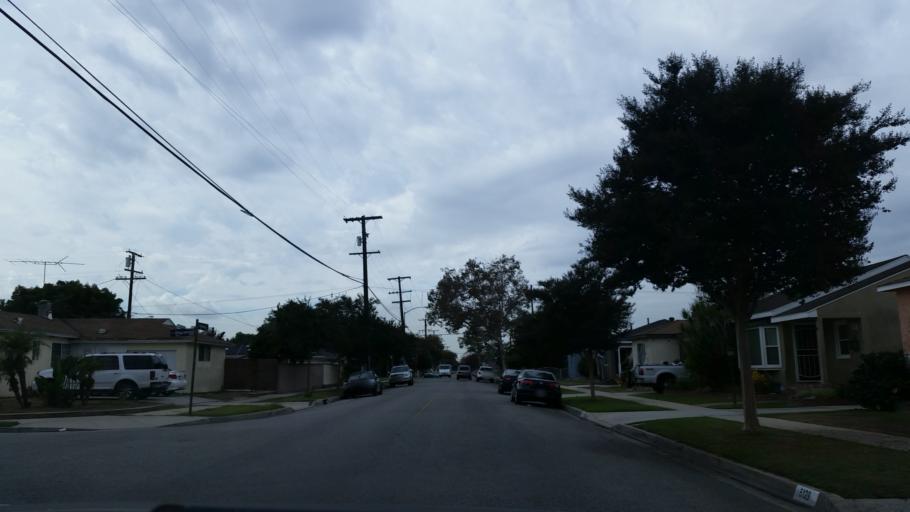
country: US
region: California
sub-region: Los Angeles County
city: Lakewood
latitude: 33.8642
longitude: -118.1326
